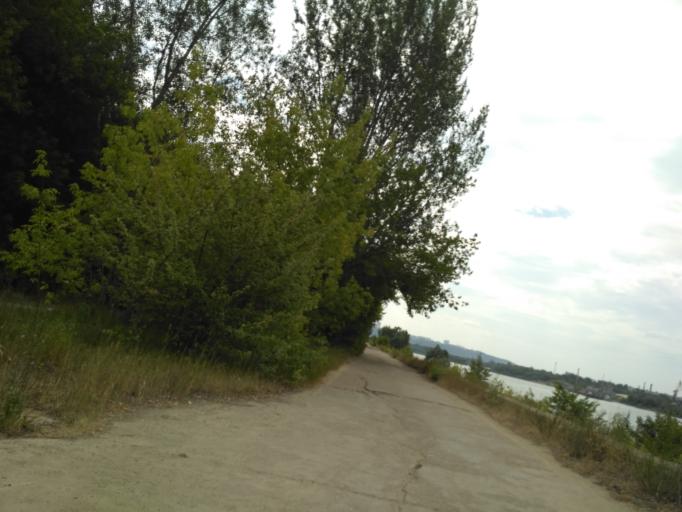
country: RU
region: Nizjnij Novgorod
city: Nizhniy Novgorod
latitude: 56.2973
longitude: 43.9672
